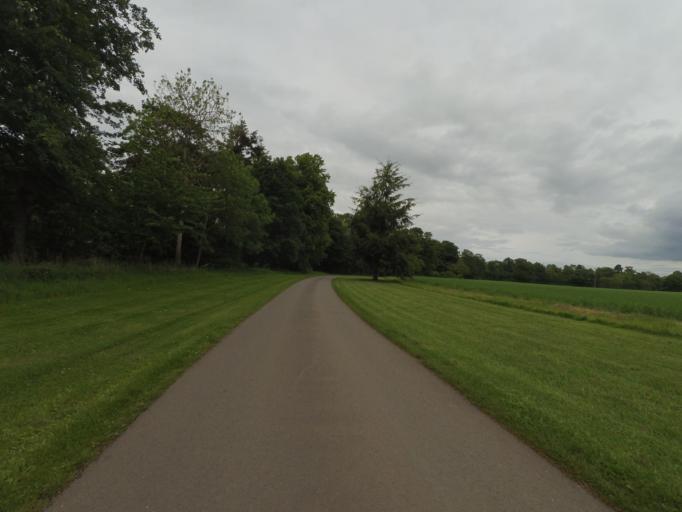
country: GB
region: Scotland
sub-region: East Lothian
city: Pencaitland
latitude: 55.9149
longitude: -2.8979
